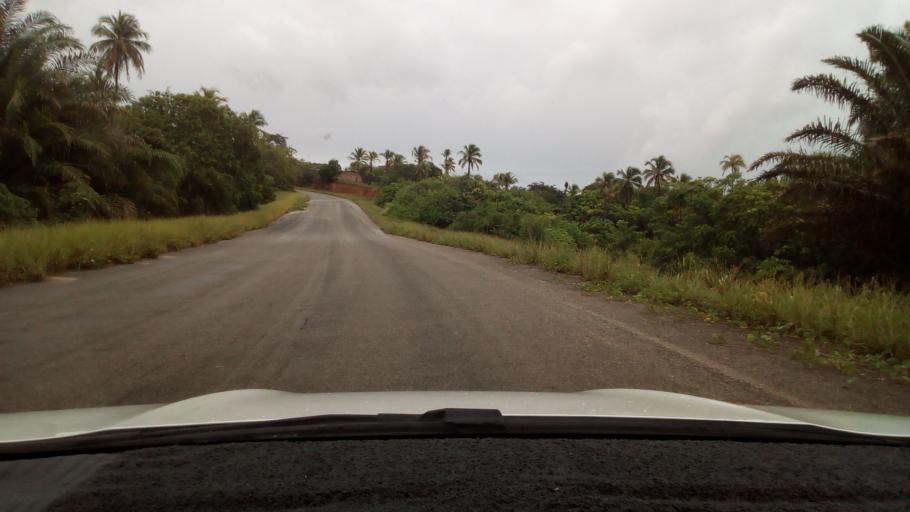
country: BR
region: Paraiba
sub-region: Pitimbu
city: Pitimbu
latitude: -7.4464
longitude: -34.8352
